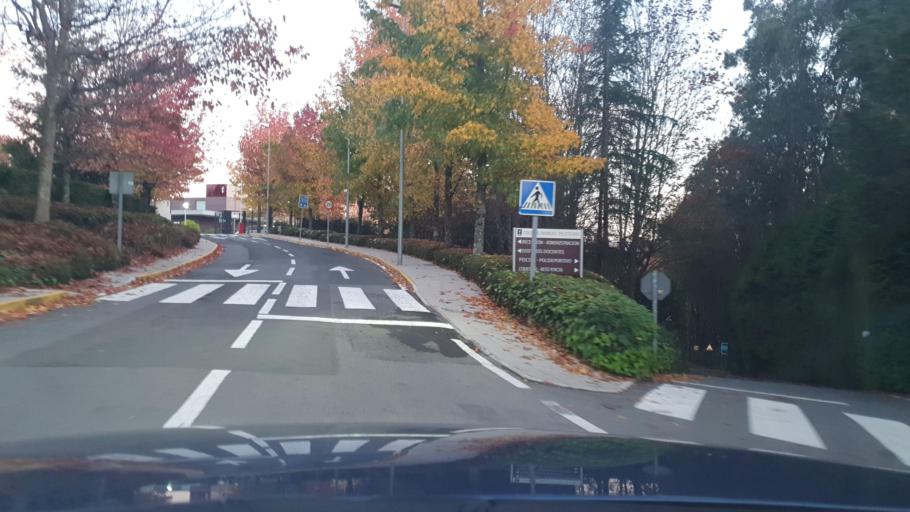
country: ES
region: Galicia
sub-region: Provincia da Coruna
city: Santiago de Compostela
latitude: 42.8523
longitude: -8.5371
